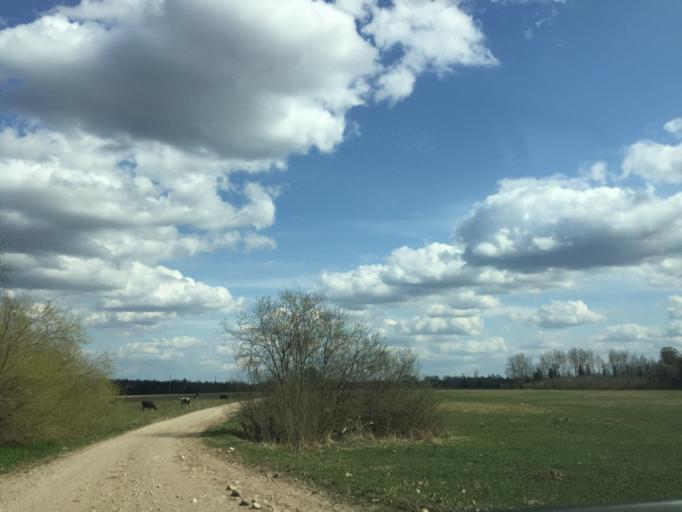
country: LV
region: Skriveri
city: Skriveri
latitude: 56.7590
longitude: 25.1420
